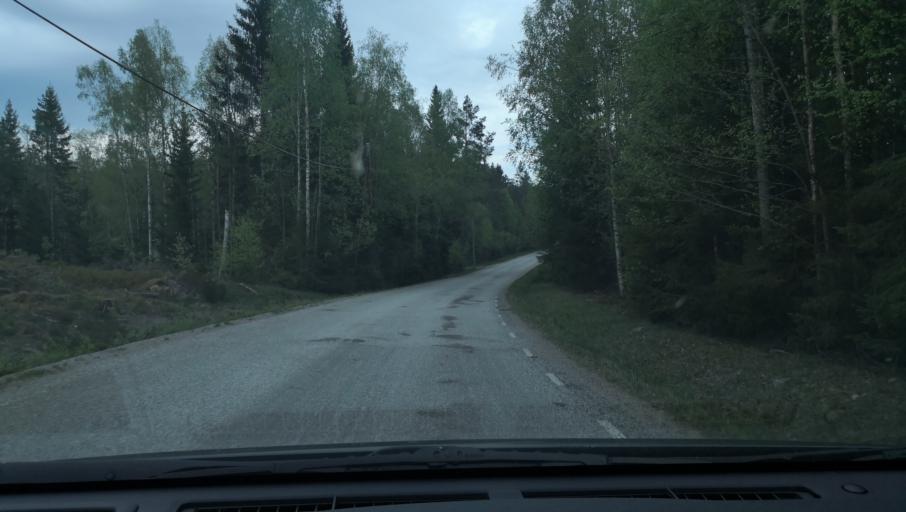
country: SE
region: Vaestmanland
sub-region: Skinnskattebergs Kommun
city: Skinnskatteberg
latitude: 59.8199
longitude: 15.5521
